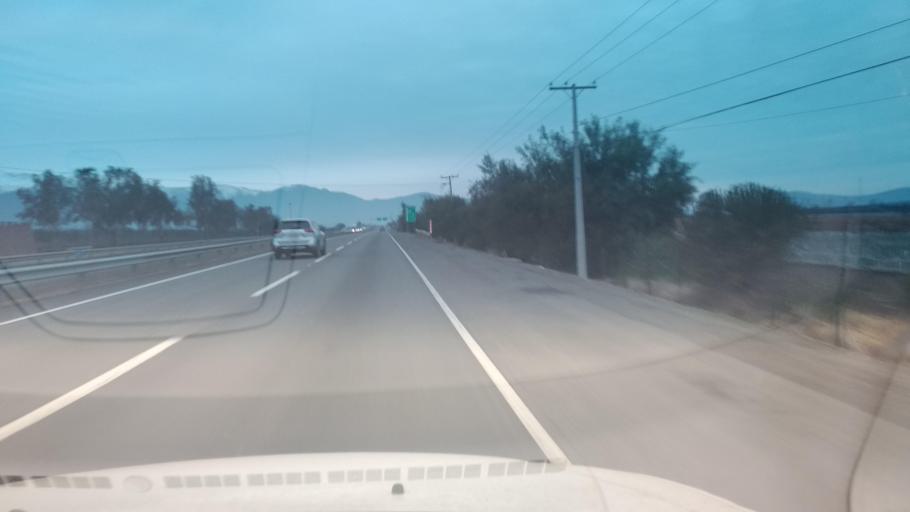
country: CL
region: Santiago Metropolitan
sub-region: Provincia de Chacabuco
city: Chicureo Abajo
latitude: -33.1410
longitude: -70.6623
